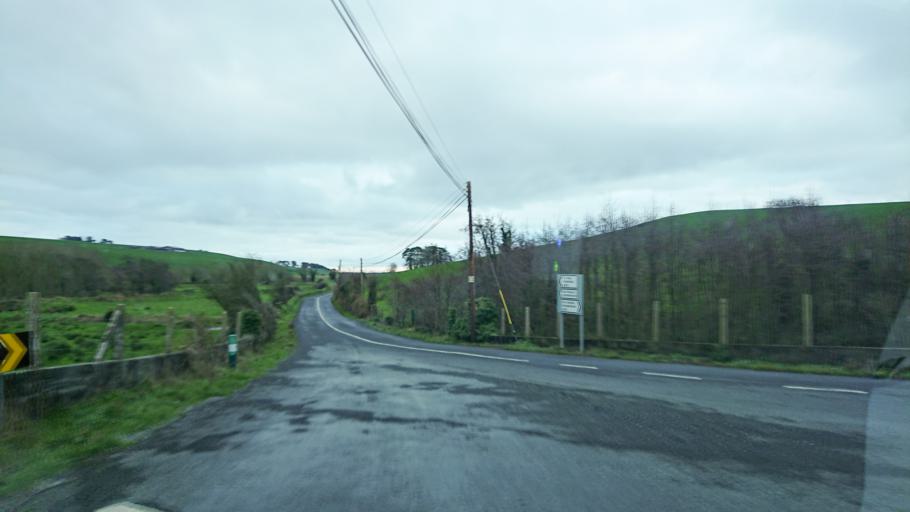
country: IE
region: Munster
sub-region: Waterford
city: Portlaw
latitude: 52.1537
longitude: -7.3825
